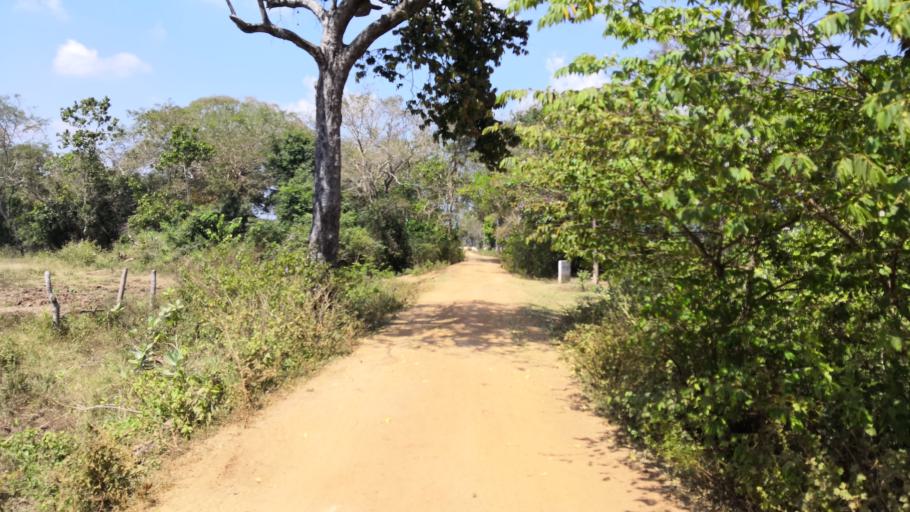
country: LK
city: Padaviya Divisional Secretariat
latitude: 8.9721
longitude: 80.6819
